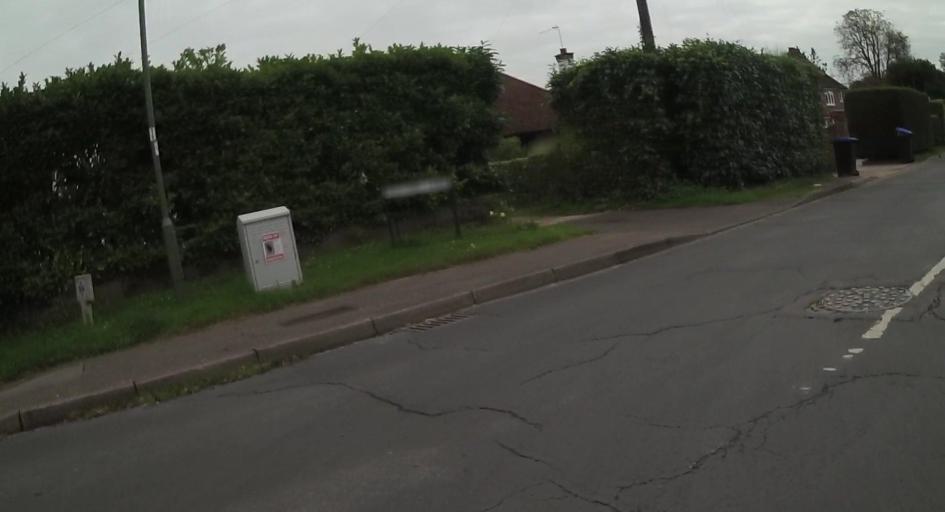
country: GB
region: England
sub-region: Surrey
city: West Byfleet
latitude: 51.3231
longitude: -0.5056
